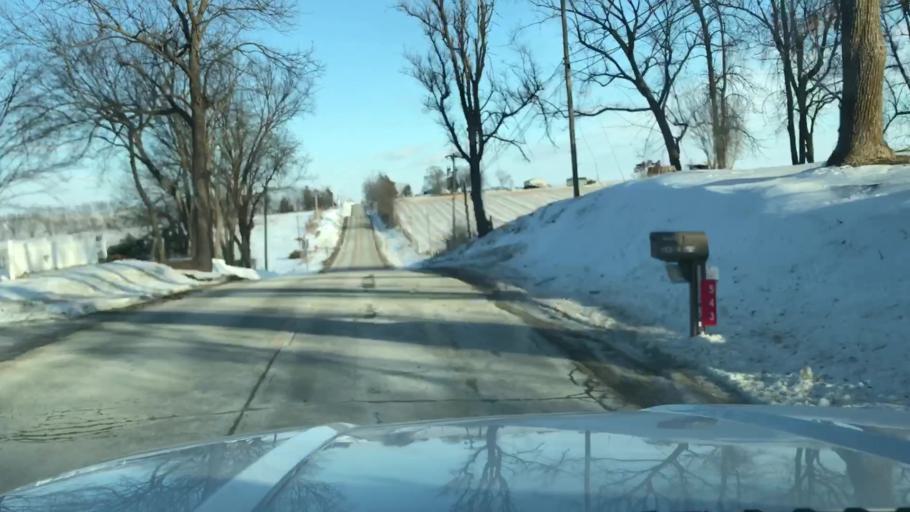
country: US
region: Missouri
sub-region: Andrew County
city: Savannah
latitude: 40.0251
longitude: -94.9690
